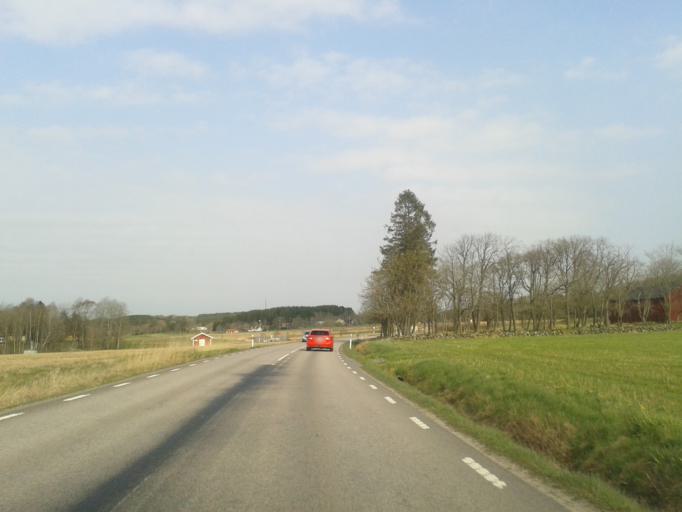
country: SE
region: Vaestra Goetaland
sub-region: Kungalvs Kommun
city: Kode
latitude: 57.8792
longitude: 11.8962
